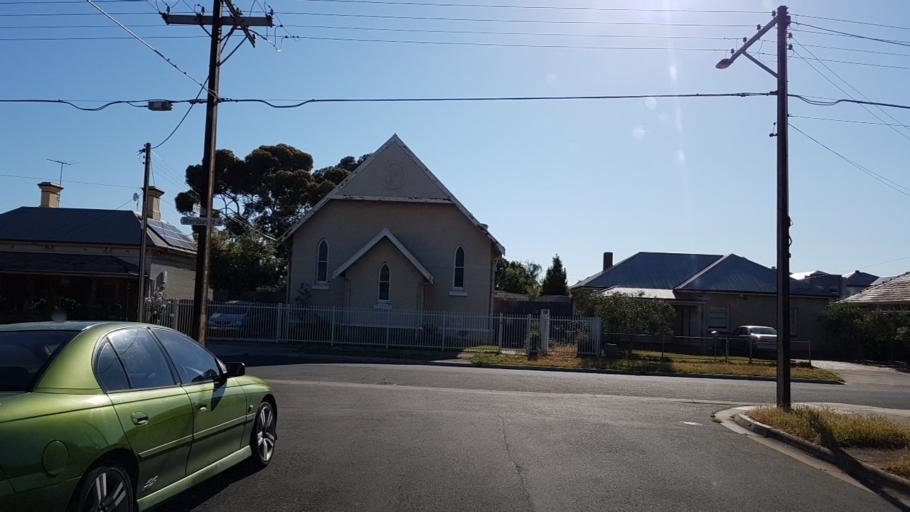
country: AU
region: South Australia
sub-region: Charles Sturt
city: Woodville North
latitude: -34.8689
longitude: 138.5424
